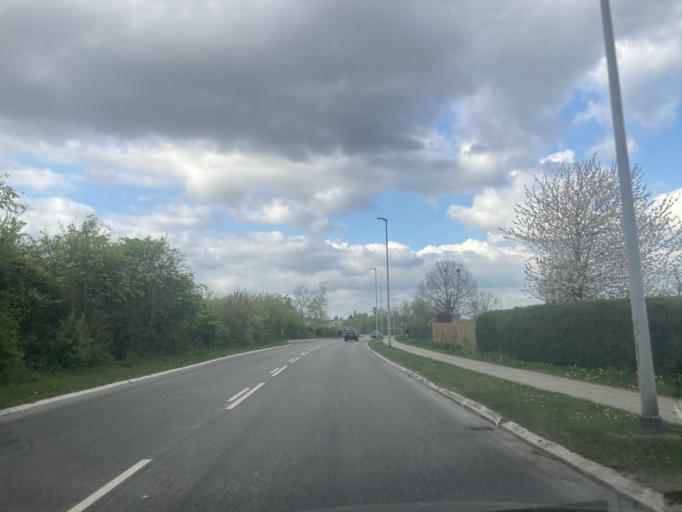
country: DK
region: Zealand
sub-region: Greve Kommune
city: Tune
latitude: 55.5978
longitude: 12.1768
